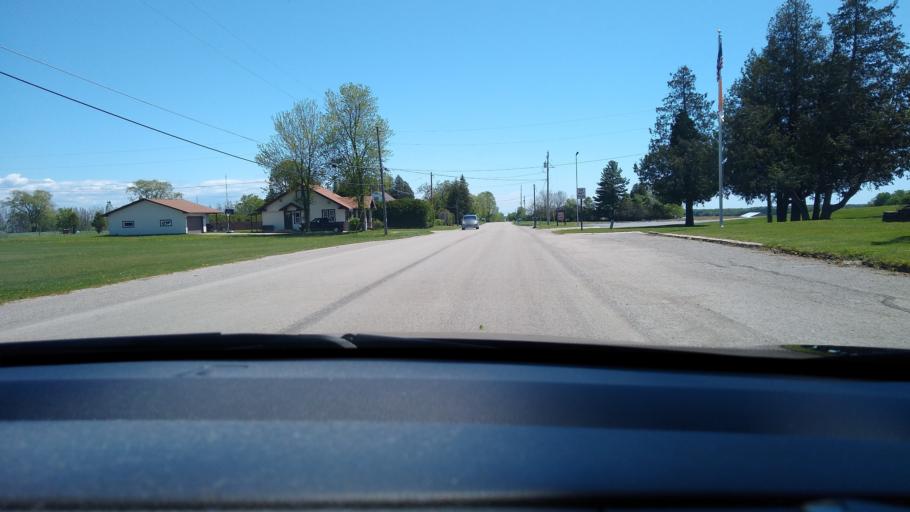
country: US
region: Michigan
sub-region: Delta County
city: Escanaba
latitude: 45.8261
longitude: -87.1676
